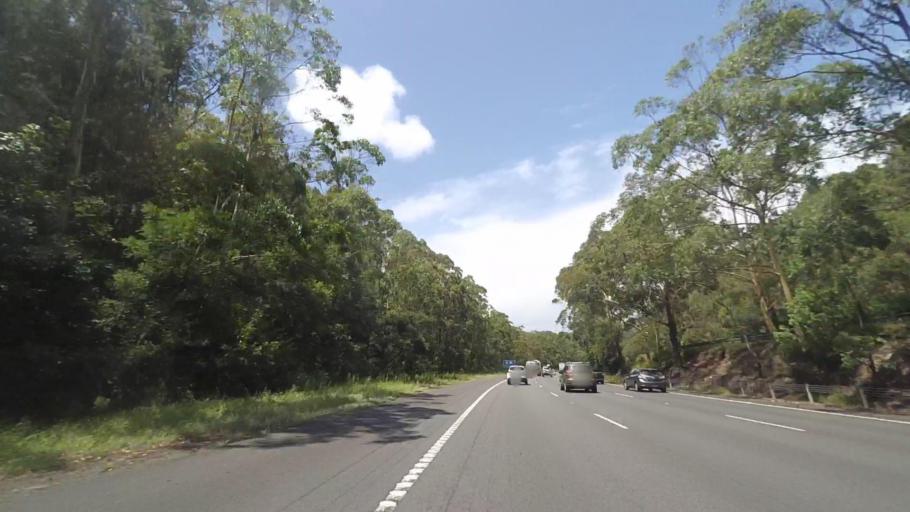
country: AU
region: New South Wales
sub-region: Gosford Shire
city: Lisarow
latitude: -33.3526
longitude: 151.3570
